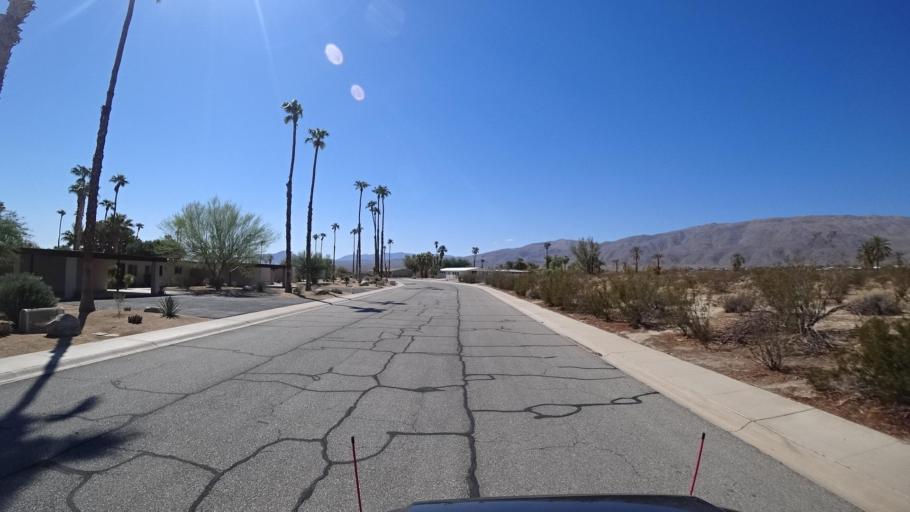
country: US
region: California
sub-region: San Diego County
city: Borrego Springs
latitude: 33.2330
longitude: -116.3580
